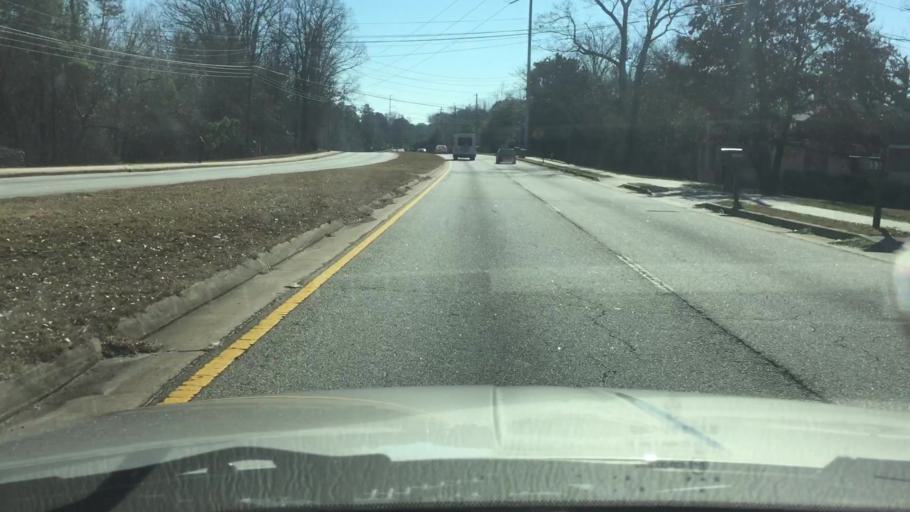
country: US
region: Georgia
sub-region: DeKalb County
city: Stone Mountain
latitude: 33.7556
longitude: -84.1973
